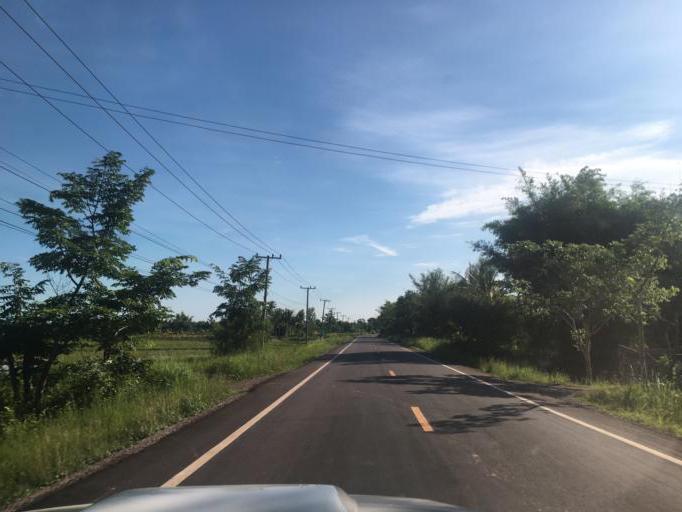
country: TH
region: Changwat Udon Thani
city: Kut Chap
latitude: 17.4881
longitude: 102.5965
